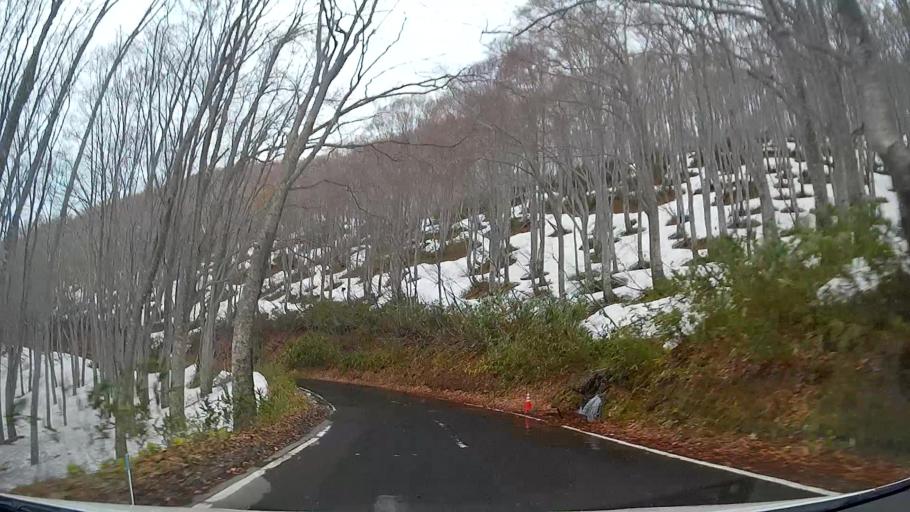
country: JP
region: Aomori
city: Aomori Shi
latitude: 40.6514
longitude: 140.8443
